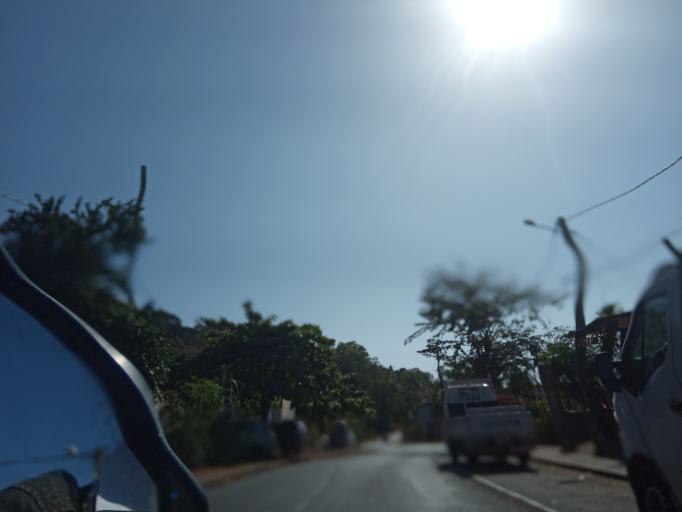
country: YT
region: Bandrele
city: Bandrele
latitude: -12.8928
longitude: 45.2027
